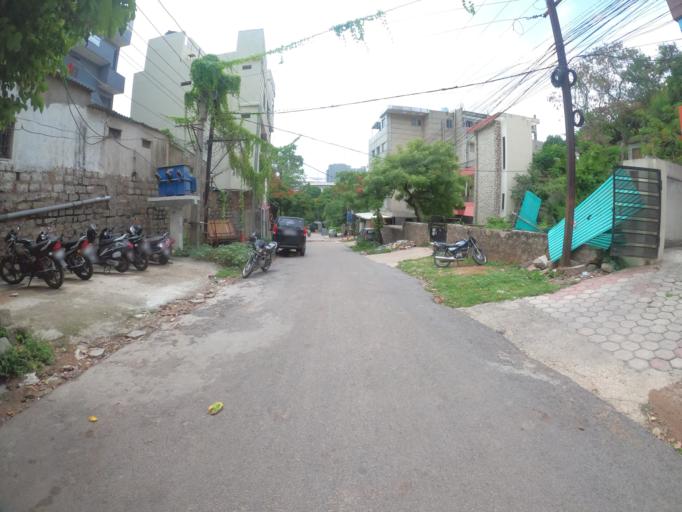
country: IN
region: Telangana
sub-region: Hyderabad
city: Hyderabad
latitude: 17.4280
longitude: 78.4495
